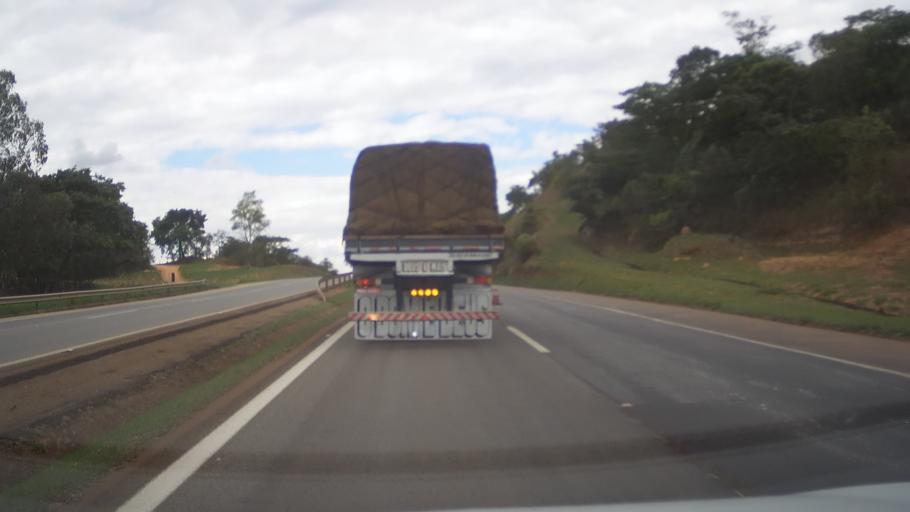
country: BR
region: Minas Gerais
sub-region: Itauna
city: Itauna
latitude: -20.3174
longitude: -44.4535
